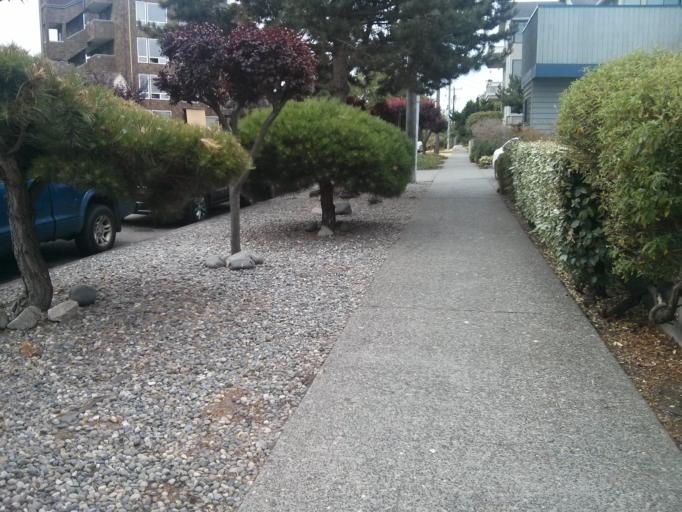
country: US
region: Washington
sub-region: King County
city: White Center
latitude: 47.5785
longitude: -122.4122
